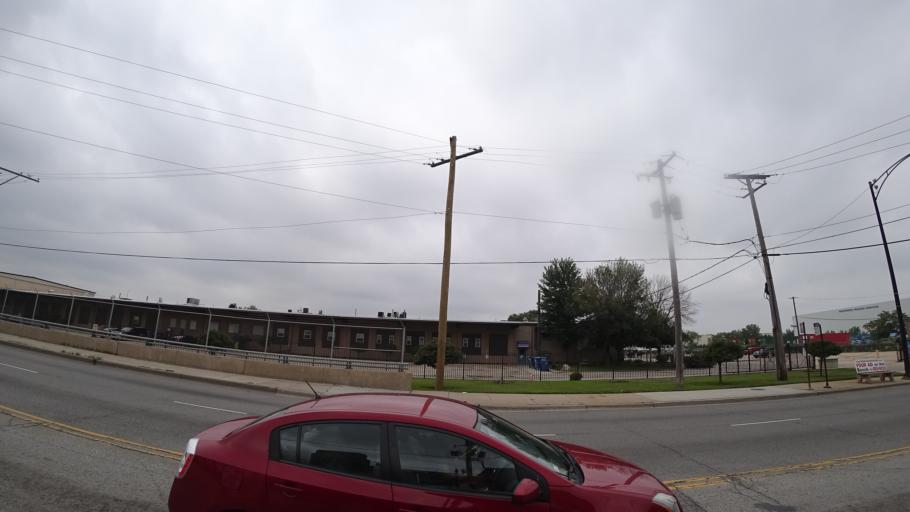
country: US
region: Illinois
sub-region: Cook County
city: Chicago
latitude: 41.8436
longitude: -87.6750
